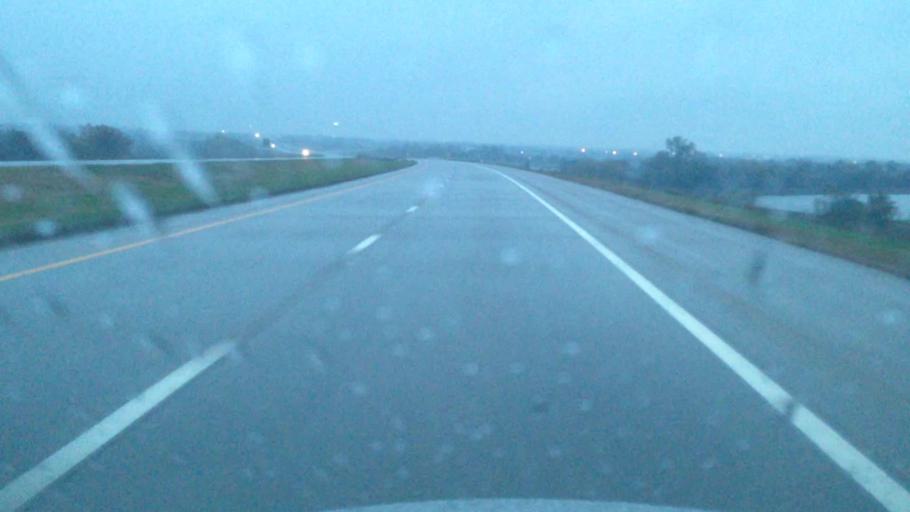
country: US
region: Kansas
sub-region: Franklin County
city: Ottawa
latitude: 38.6746
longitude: -95.2607
